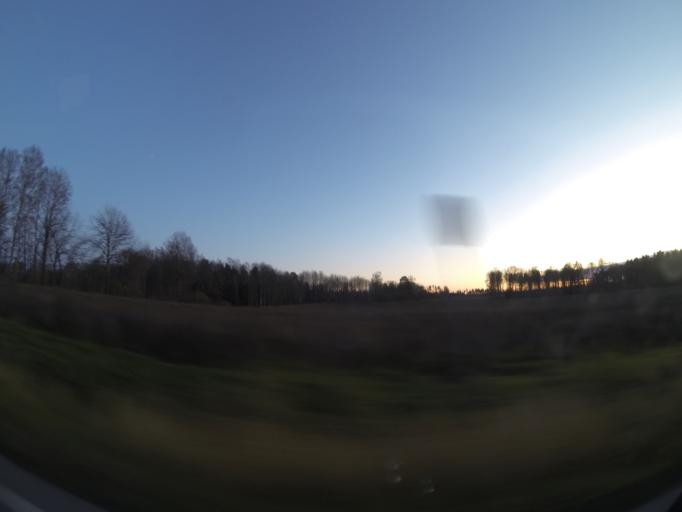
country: SE
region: OErebro
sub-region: Lindesbergs Kommun
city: Fellingsbro
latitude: 59.3262
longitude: 15.4715
